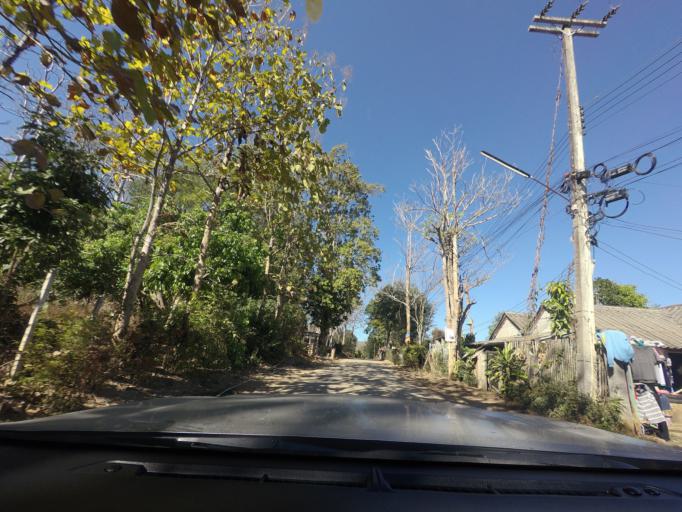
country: TH
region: Mae Hong Son
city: Wiang Nuea
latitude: 19.3976
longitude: 98.4217
